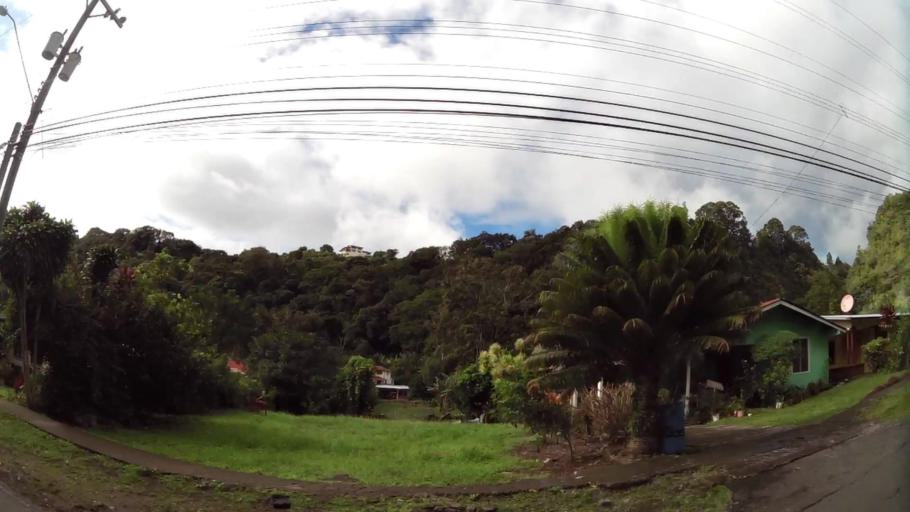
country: PA
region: Chiriqui
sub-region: Distrito Boquete
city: Boquete
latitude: 8.7957
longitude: -82.4475
